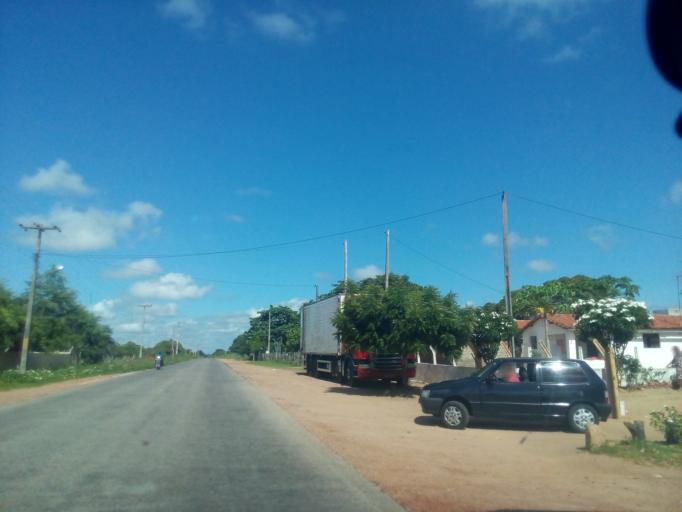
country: BR
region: Rio Grande do Norte
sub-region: Sao Paulo Do Potengi
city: Sao Paulo do Potengi
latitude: -5.9154
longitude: -35.7112
